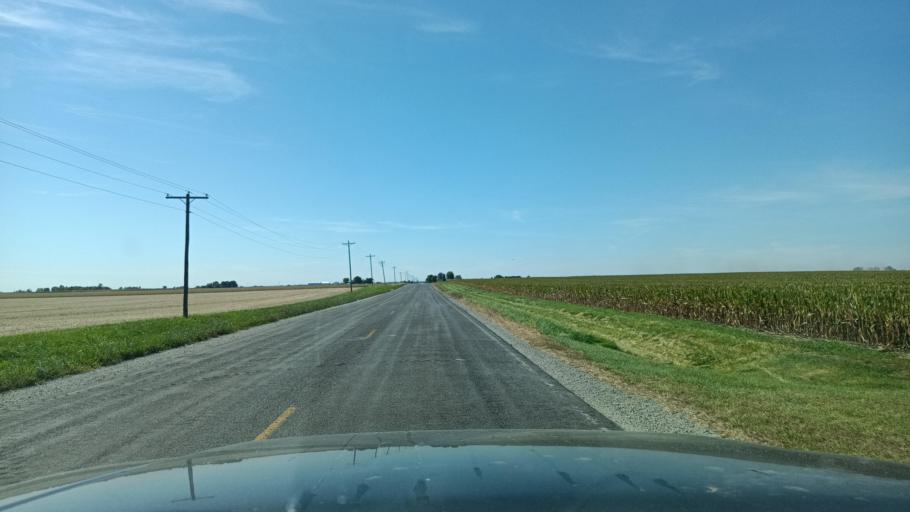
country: US
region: Illinois
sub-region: De Witt County
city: Farmer City
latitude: 40.2239
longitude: -88.7227
